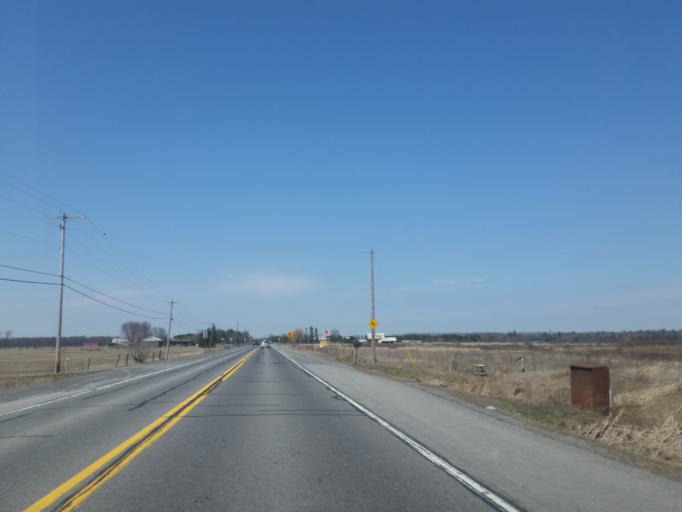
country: CA
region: Ontario
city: Bells Corners
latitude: 45.4259
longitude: -76.0254
